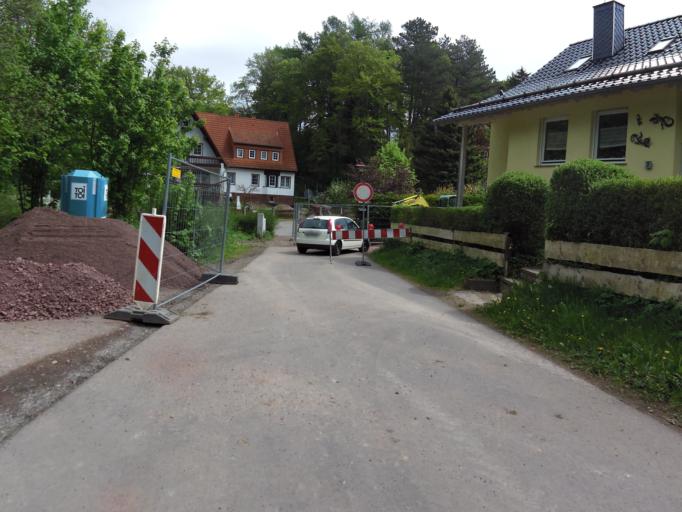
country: DE
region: Thuringia
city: Georgenthal
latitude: 50.8269
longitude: 10.6611
